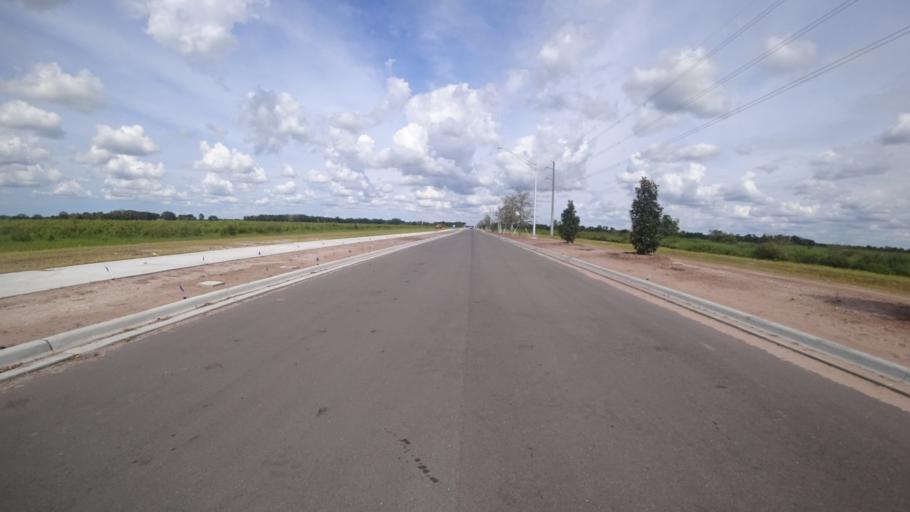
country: US
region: Florida
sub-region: Sarasota County
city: The Meadows
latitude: 27.4506
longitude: -82.3510
